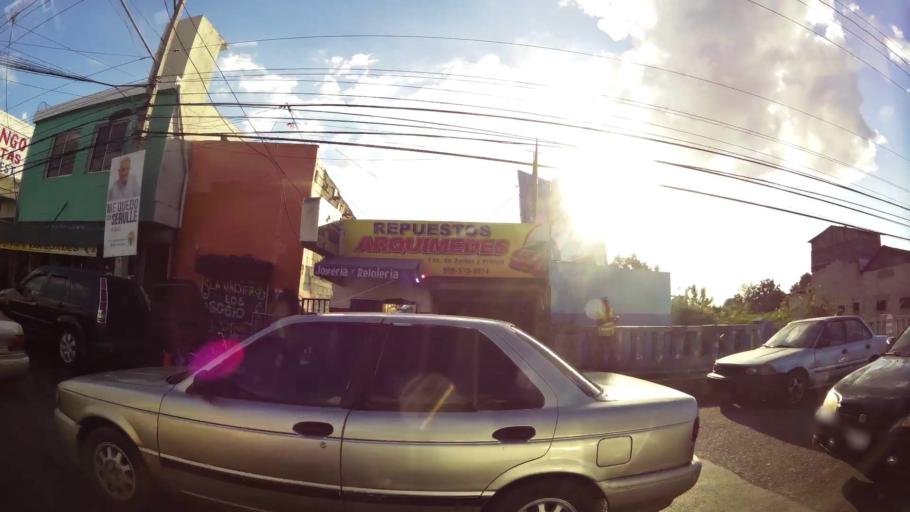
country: DO
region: Santiago
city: Santiago de los Caballeros
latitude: 19.4704
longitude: -70.7109
